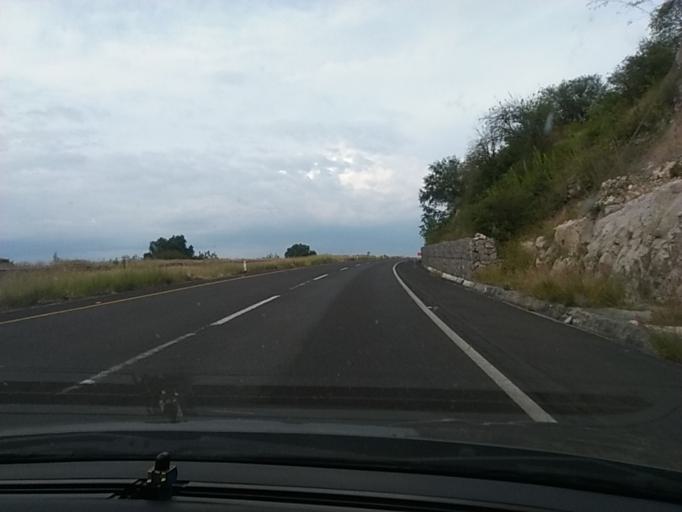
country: MX
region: Mexico
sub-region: Chapultepec
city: Chucandiro
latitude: 19.8984
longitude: -101.3038
